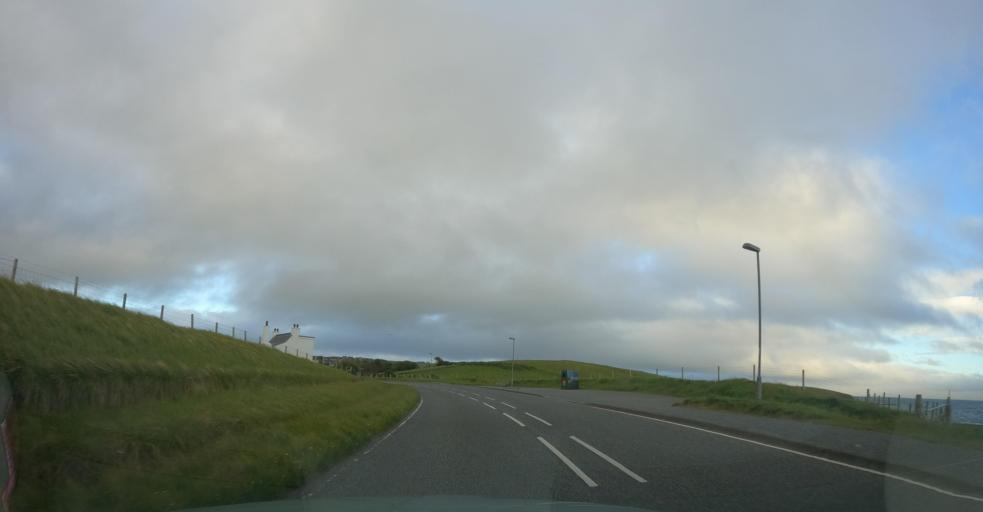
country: GB
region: Scotland
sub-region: Eilean Siar
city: Stornoway
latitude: 58.2049
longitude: -6.2850
